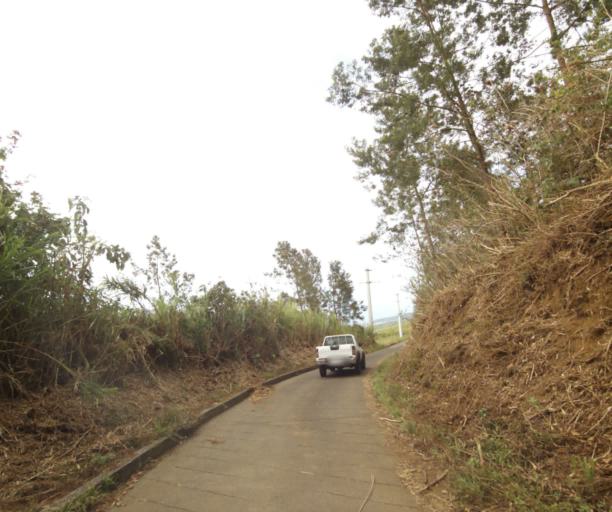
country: RE
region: Reunion
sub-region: Reunion
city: Saint-Paul
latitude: -21.0089
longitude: 55.3485
